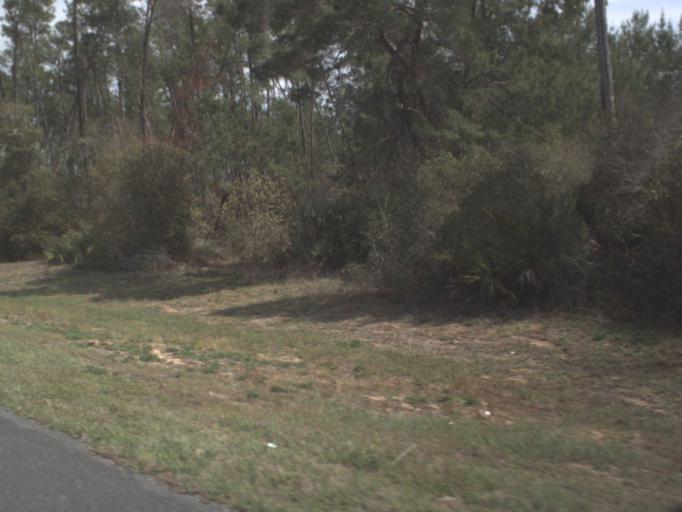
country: US
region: Florida
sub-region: Lake County
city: Astor
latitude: 29.2043
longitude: -81.6592
